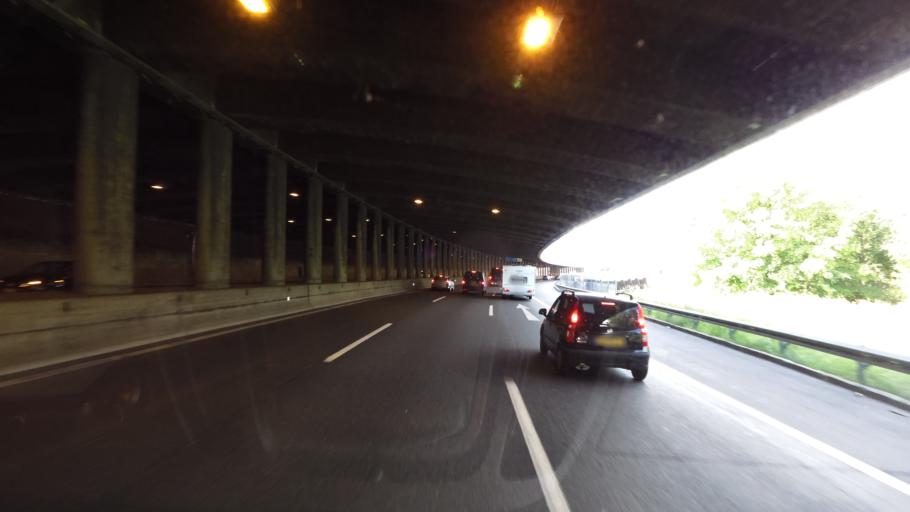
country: AT
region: Tyrol
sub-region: Politischer Bezirk Innsbruck Land
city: Schoenberg im Stubaital
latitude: 47.1871
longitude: 11.4018
